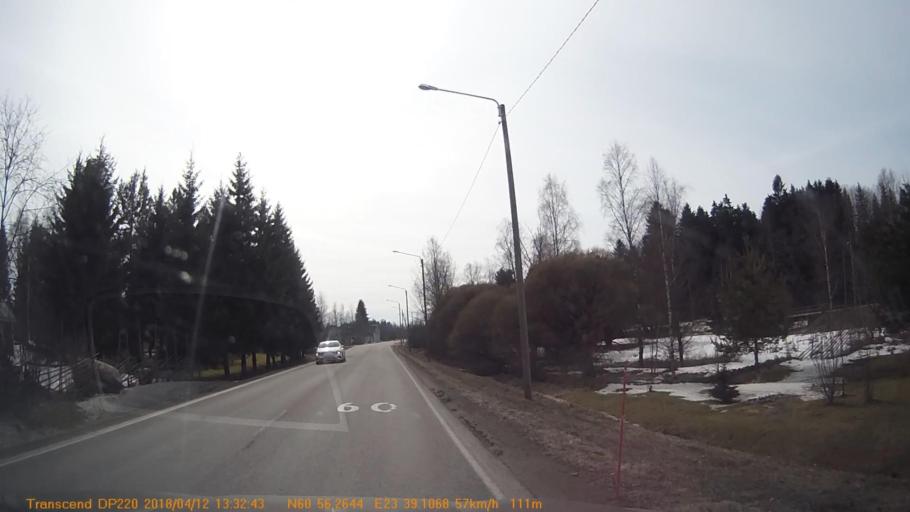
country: FI
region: Haeme
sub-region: Forssa
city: Forssa
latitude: 60.9377
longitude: 23.6517
